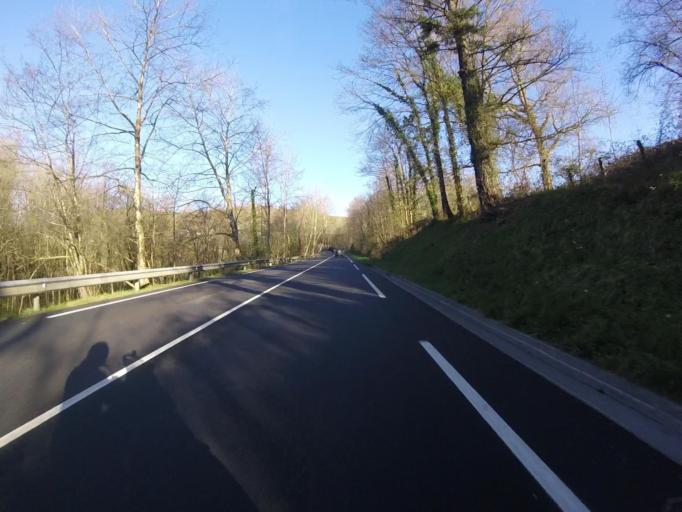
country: ES
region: Basque Country
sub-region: Provincia de Guipuzcoa
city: Errenteria
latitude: 43.2836
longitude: -1.9062
